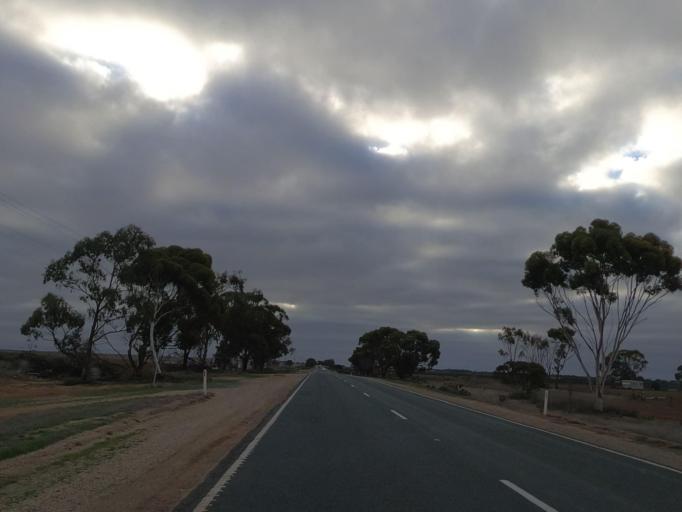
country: AU
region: Victoria
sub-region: Swan Hill
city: Swan Hill
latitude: -35.6406
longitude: 143.8286
